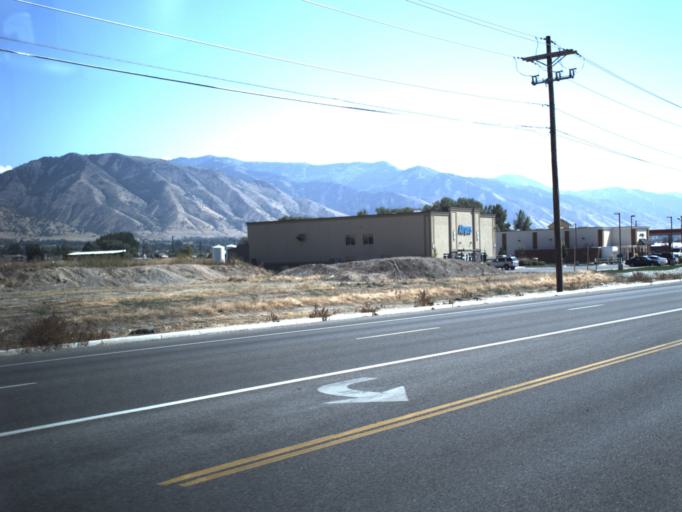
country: US
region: Utah
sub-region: Cache County
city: Hyde Park
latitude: 41.8017
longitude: -111.8335
